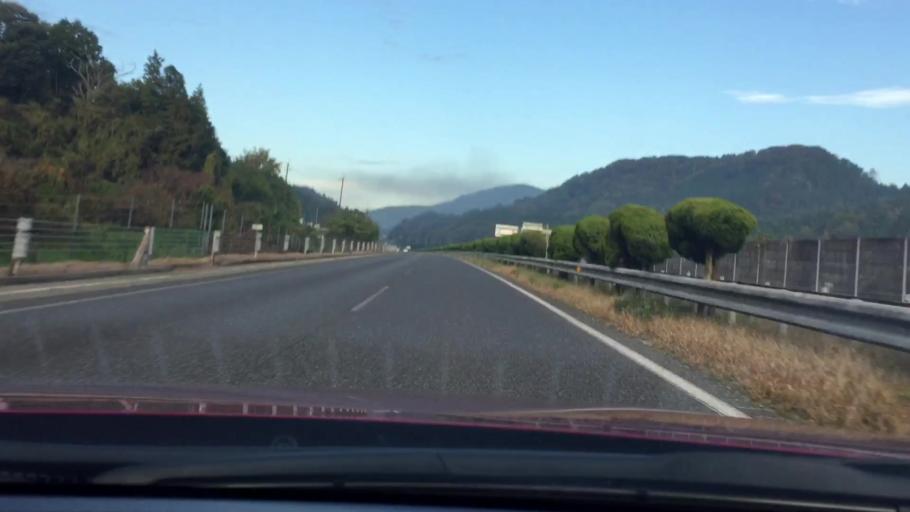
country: JP
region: Hyogo
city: Yamazakicho-nakabirose
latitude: 34.9695
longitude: 134.6705
